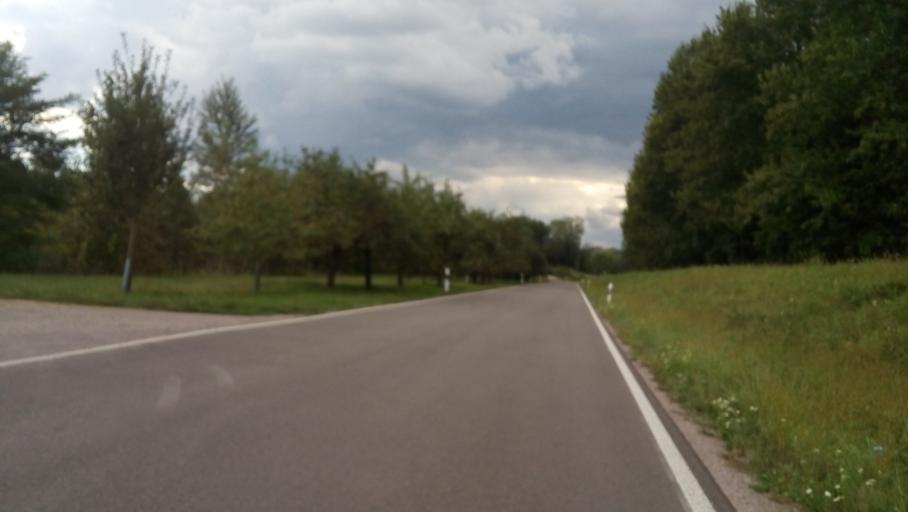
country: DE
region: Baden-Wuerttemberg
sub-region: Karlsruhe Region
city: Greffern
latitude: 48.7491
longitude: 7.9918
